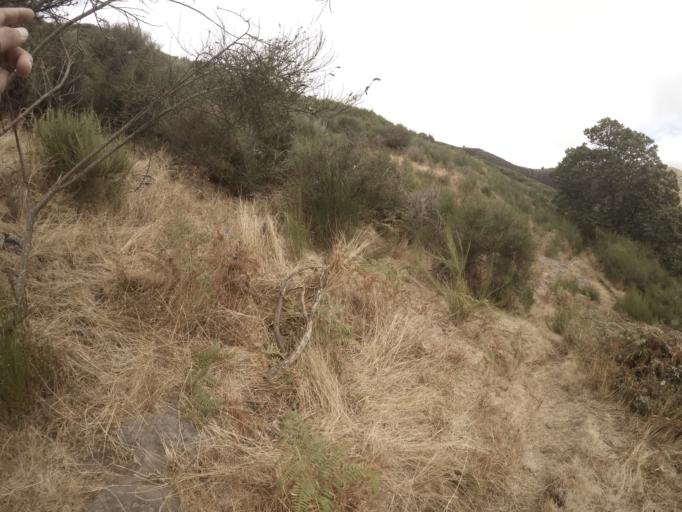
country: PT
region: Madeira
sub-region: Camara de Lobos
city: Curral das Freiras
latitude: 32.7086
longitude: -17.0088
